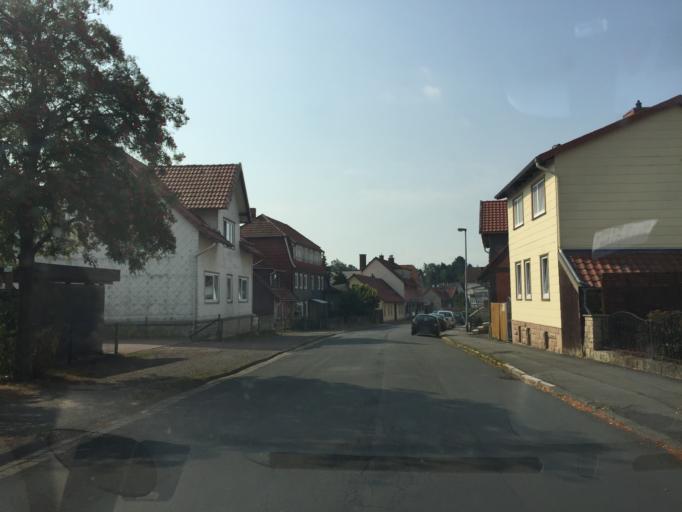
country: DE
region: Lower Saxony
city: Bad Sachsa
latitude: 51.5954
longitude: 10.5621
